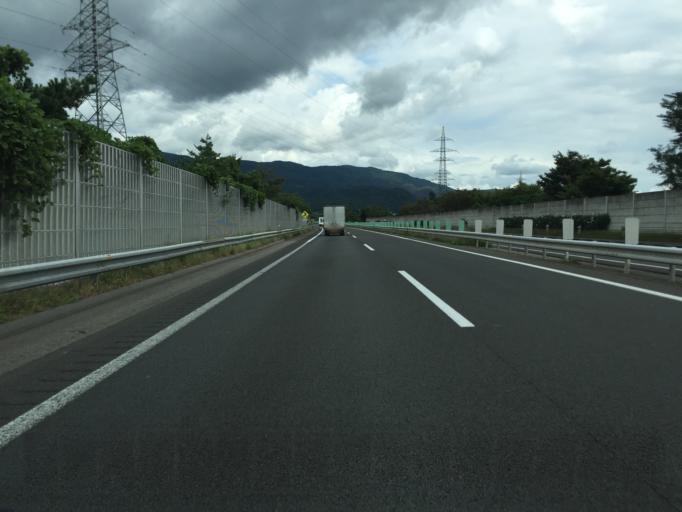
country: JP
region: Fukushima
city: Hobaramachi
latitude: 37.8657
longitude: 140.5191
